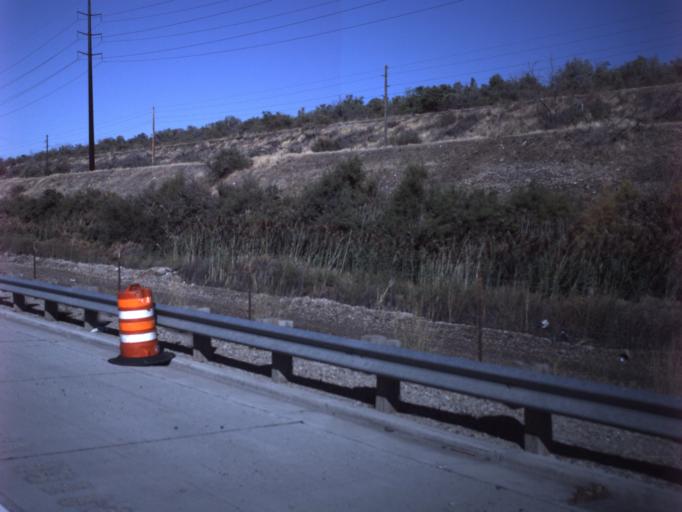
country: US
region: Utah
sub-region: Salt Lake County
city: Magna
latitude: 40.7182
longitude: -112.1057
